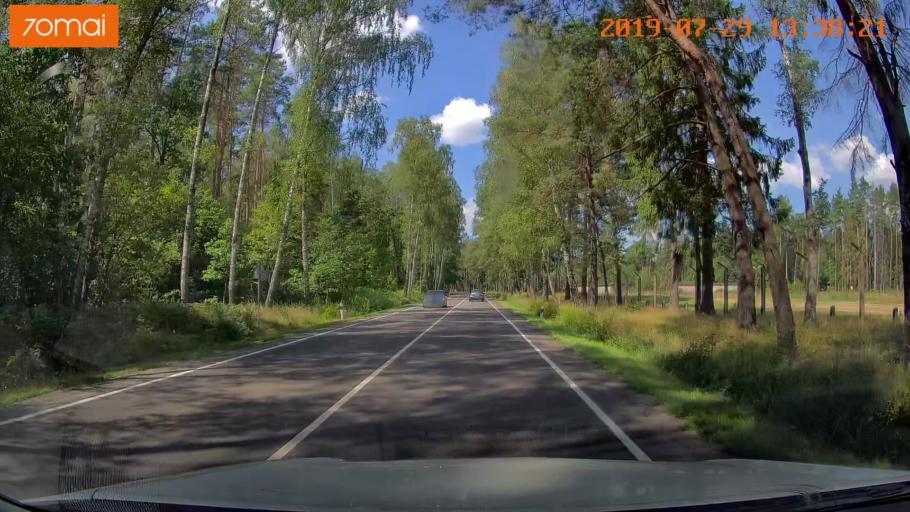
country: RU
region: Kaliningrad
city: Volochayevskoye
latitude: 54.7206
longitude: 20.1720
